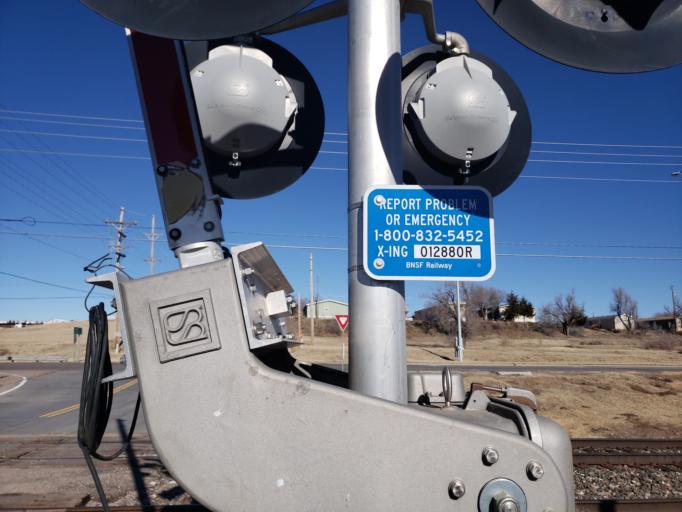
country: US
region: Kansas
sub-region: Ford County
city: Dodge City
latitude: 37.7539
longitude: -100.0512
